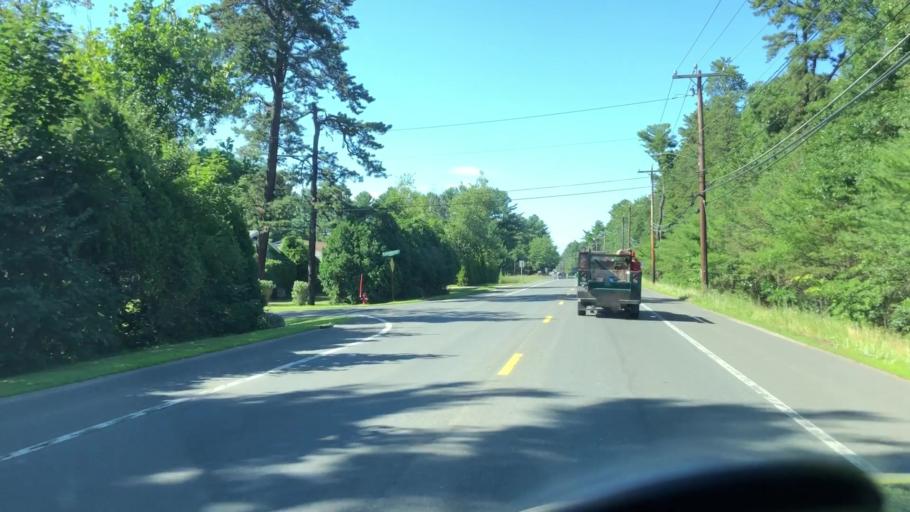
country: US
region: Massachusetts
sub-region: Hampden County
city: Westfield
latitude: 42.1621
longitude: -72.7263
